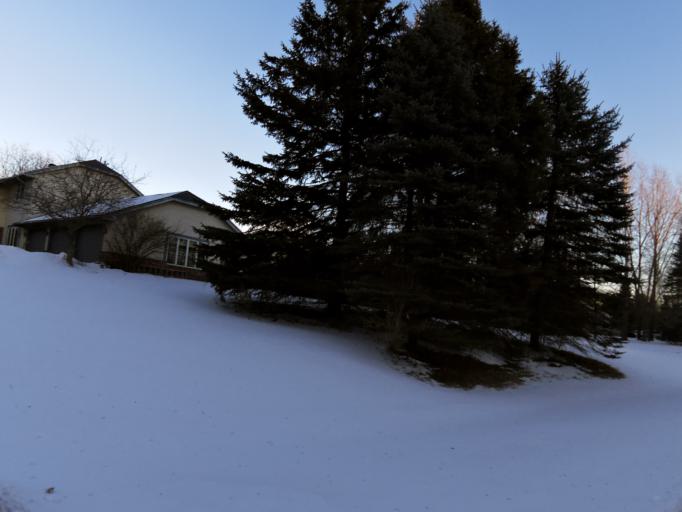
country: US
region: Minnesota
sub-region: Washington County
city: Lakeland
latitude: 44.9649
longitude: -92.8085
